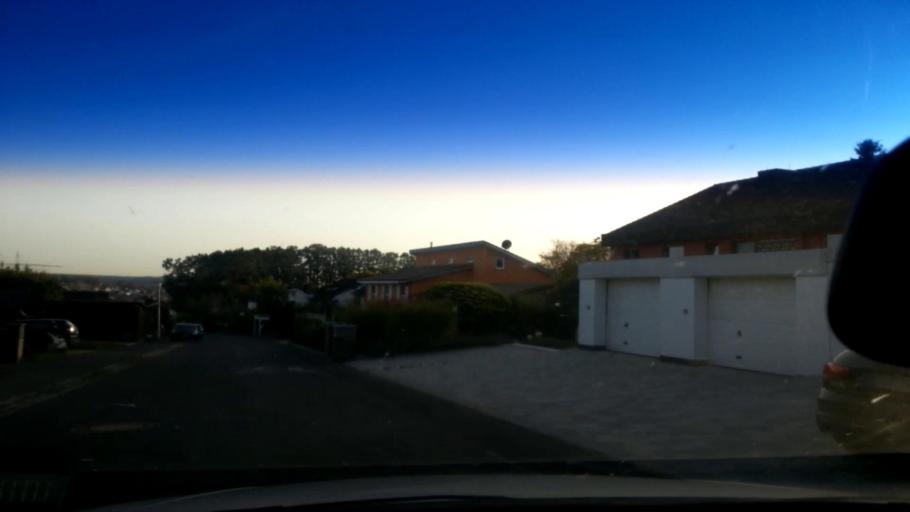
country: DE
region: Bavaria
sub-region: Upper Franconia
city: Memmelsdorf
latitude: 49.9453
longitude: 10.9561
